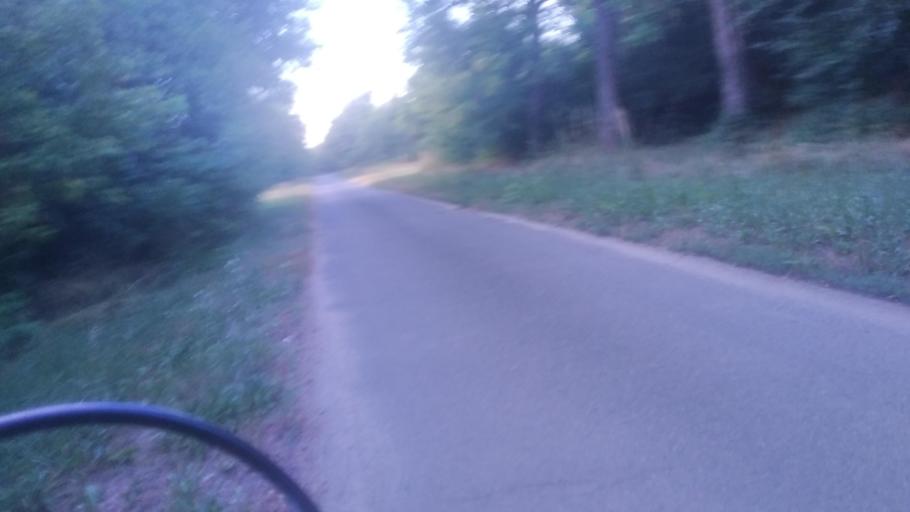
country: HU
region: Budapest
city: Budapest XVIII. keruelet
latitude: 47.4743
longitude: 19.2002
